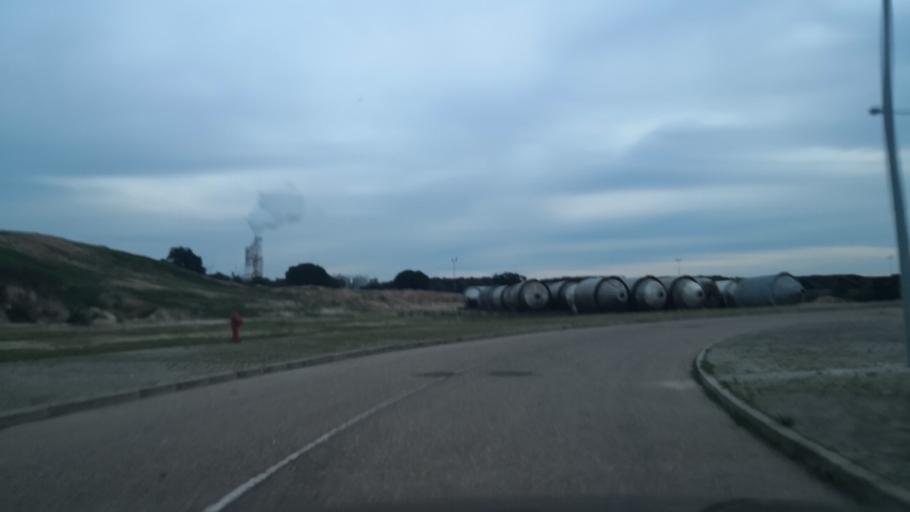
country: PT
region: Setubal
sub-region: Setubal
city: Setubal
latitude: 38.4970
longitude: -8.8143
